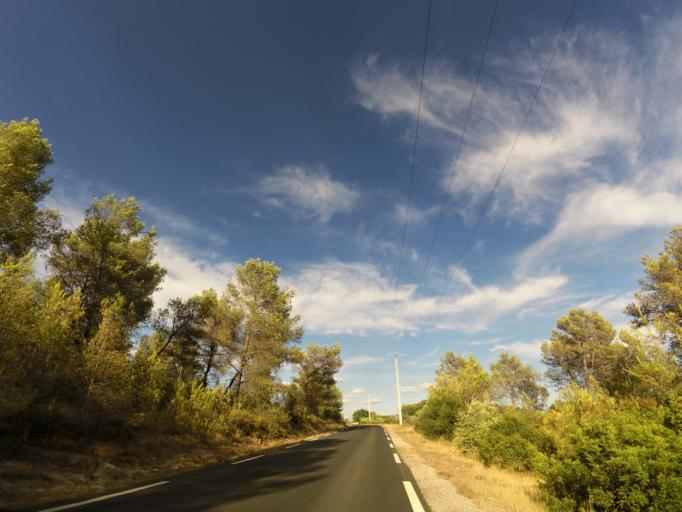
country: FR
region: Languedoc-Roussillon
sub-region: Departement de l'Herault
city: Saint-Drezery
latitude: 43.7678
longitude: 3.9878
